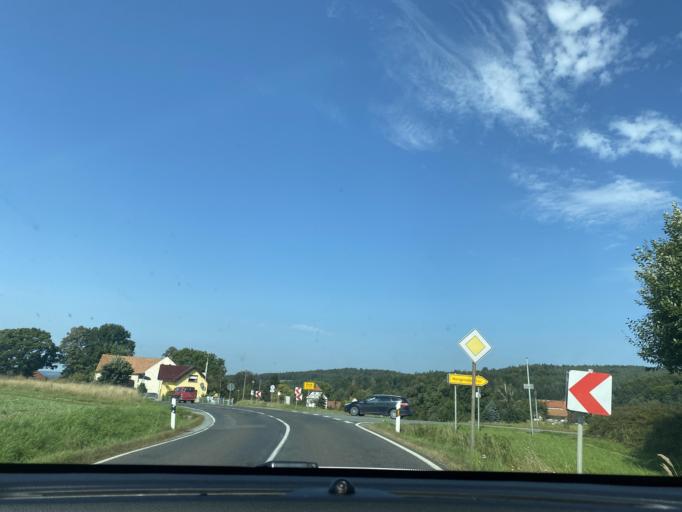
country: DE
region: Saxony
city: Reichenbach
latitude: 51.1580
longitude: 14.7957
